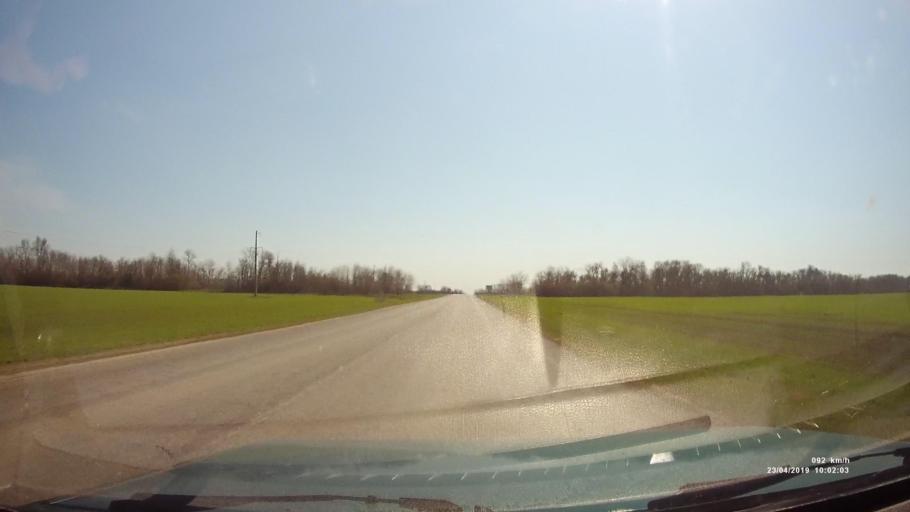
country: RU
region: Rostov
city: Sovetskoye
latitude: 46.7619
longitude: 42.1600
